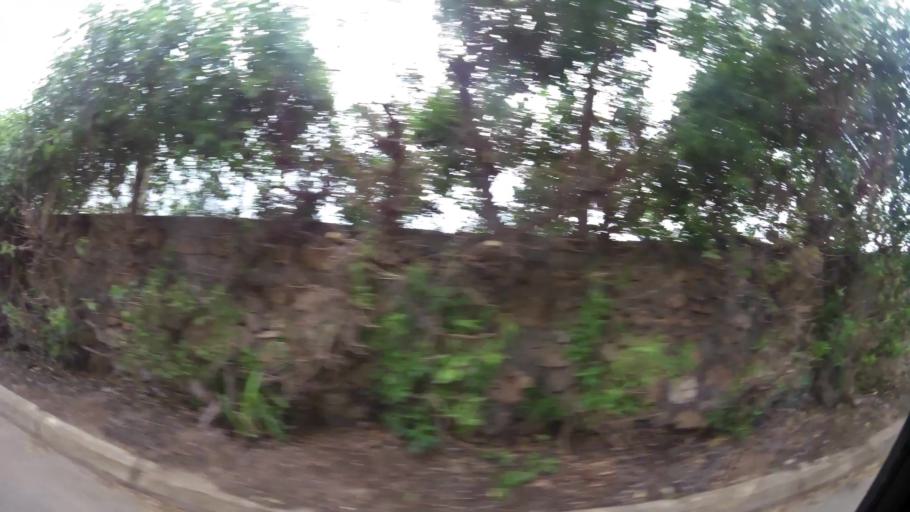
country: MA
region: Grand Casablanca
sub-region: Casablanca
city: Casablanca
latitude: 33.5844
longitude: -7.6862
